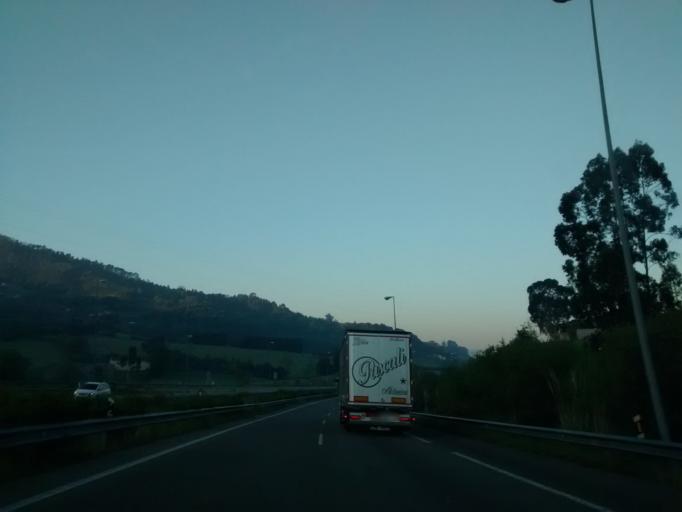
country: ES
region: Asturias
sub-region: Province of Asturias
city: Villaviciosa
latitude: 43.4969
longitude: -5.4148
